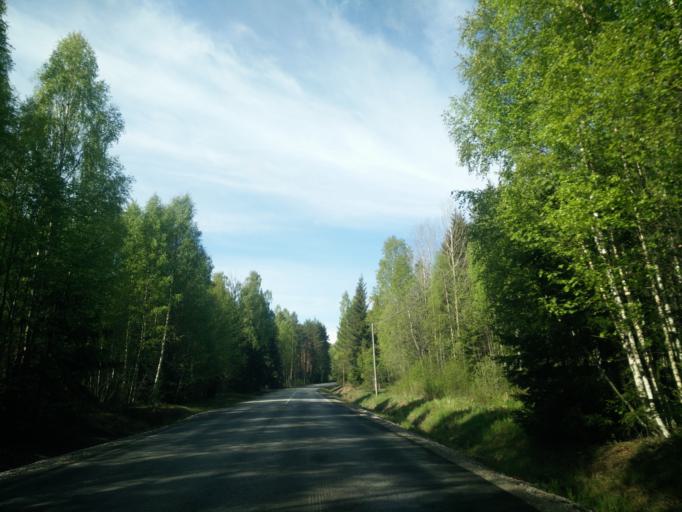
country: SE
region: Vaesternorrland
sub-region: Sundsvalls Kommun
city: Sundsvall
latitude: 62.3036
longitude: 17.2670
